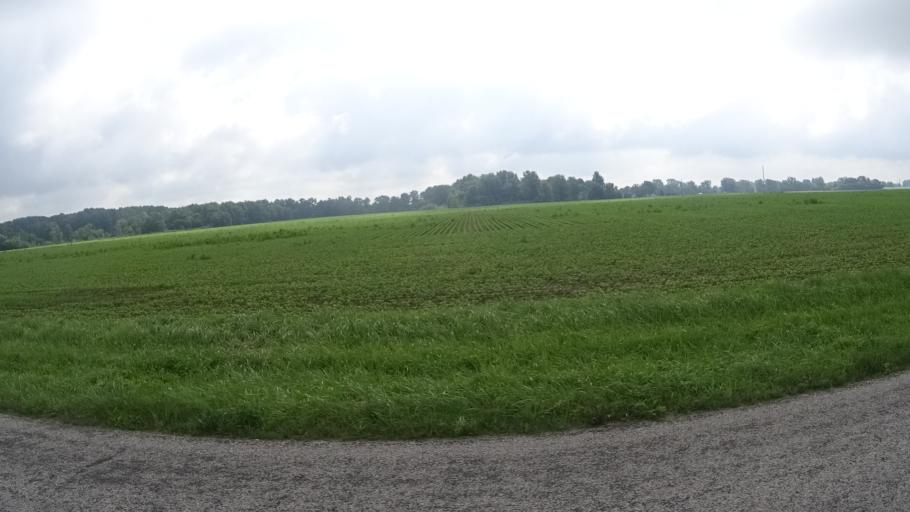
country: US
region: Ohio
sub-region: Huron County
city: Wakeman
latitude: 41.2858
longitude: -82.4808
